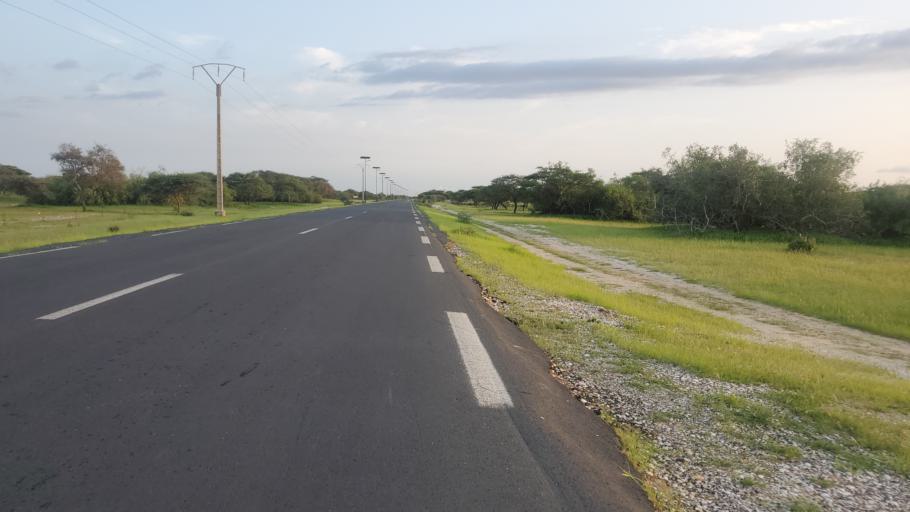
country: SN
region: Saint-Louis
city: Saint-Louis
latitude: 16.1499
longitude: -16.4098
